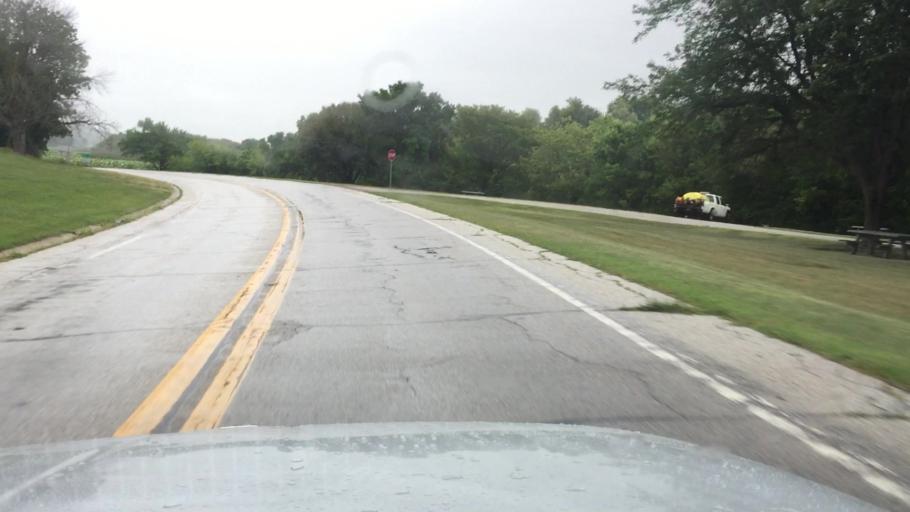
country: US
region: Illinois
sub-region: Hancock County
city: Nauvoo
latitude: 40.5395
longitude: -91.3861
